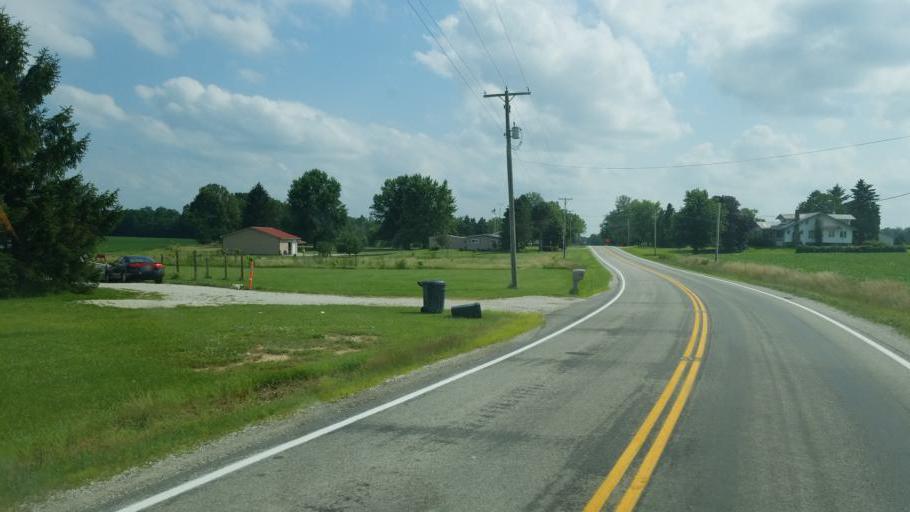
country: US
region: Ohio
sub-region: Crawford County
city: Crestline
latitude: 40.8706
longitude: -82.7733
